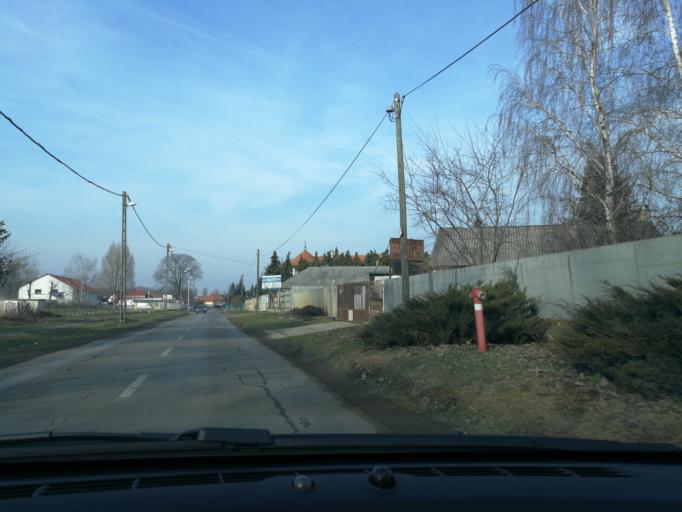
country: HU
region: Szabolcs-Szatmar-Bereg
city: Nyiregyhaza
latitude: 47.9636
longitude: 21.7344
